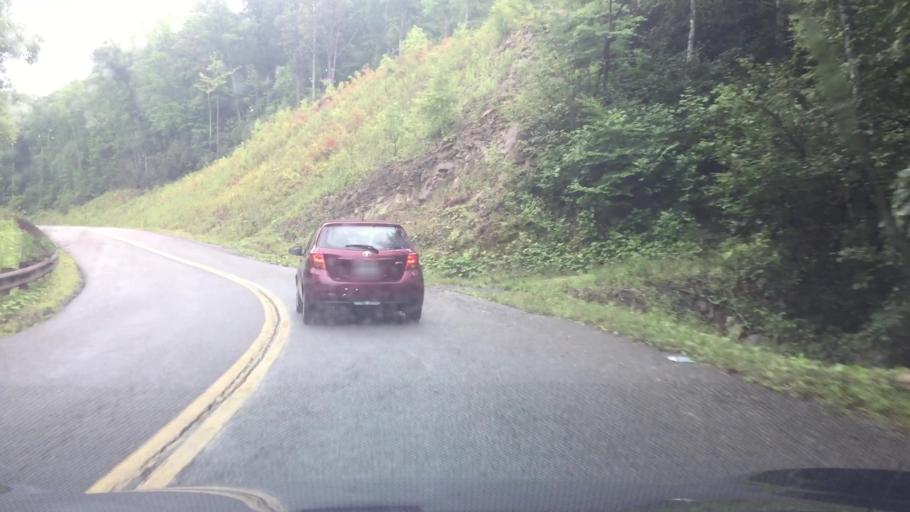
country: US
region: Virginia
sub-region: Smyth County
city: Atkins
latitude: 36.8251
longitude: -81.4150
